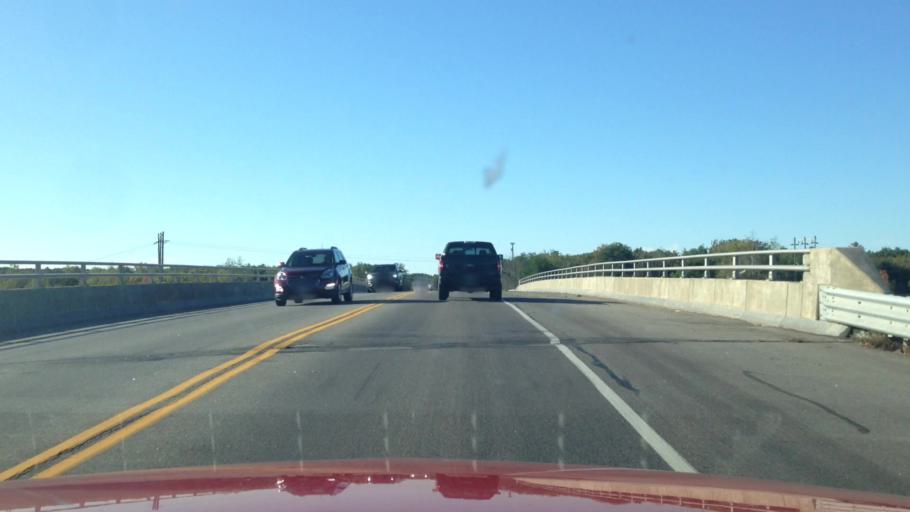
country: US
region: Maine
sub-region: Cumberland County
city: South Portland Gardens
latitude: 43.6672
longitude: -70.3307
